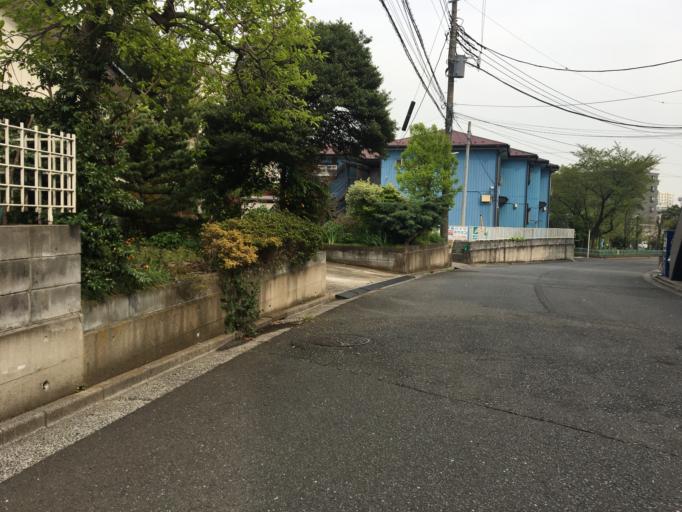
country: JP
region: Saitama
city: Shiki
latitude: 35.8344
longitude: 139.5557
